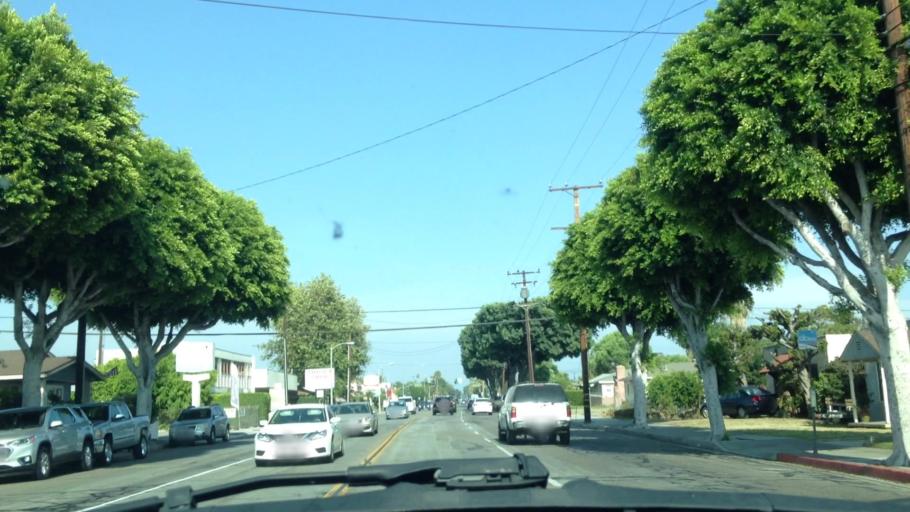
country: US
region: California
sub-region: Orange County
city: Fullerton
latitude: 33.8705
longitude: -117.9097
